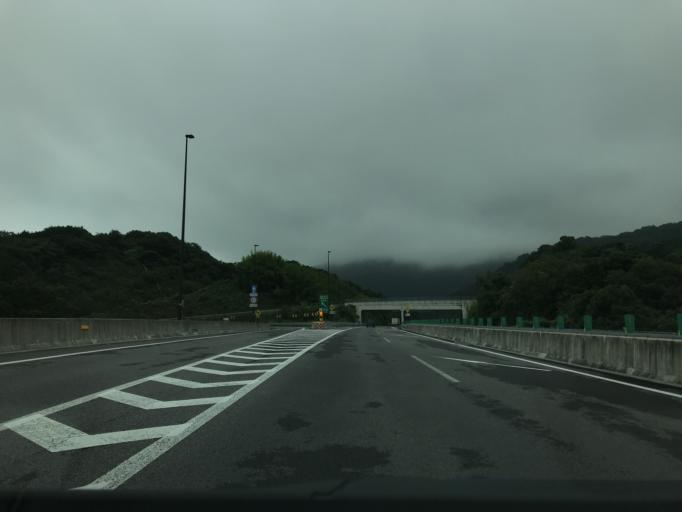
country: JP
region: Oita
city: Bungo-Takada-shi
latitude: 33.4993
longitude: 131.3165
